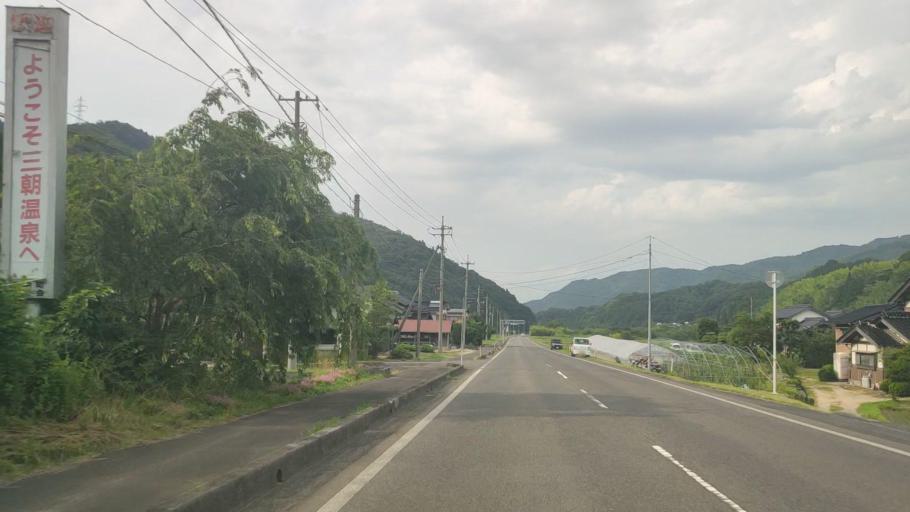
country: JP
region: Tottori
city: Kurayoshi
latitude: 35.3480
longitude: 133.8420
